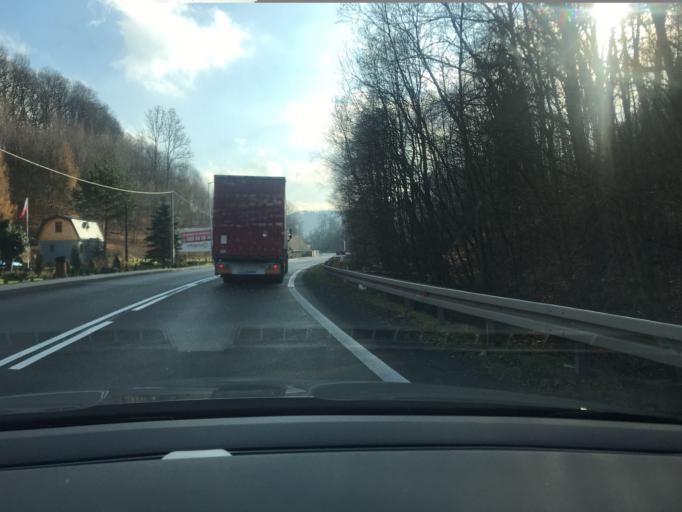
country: PL
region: Lower Silesian Voivodeship
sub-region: Powiat klodzki
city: Lewin Klodzki
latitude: 50.4164
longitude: 16.2645
